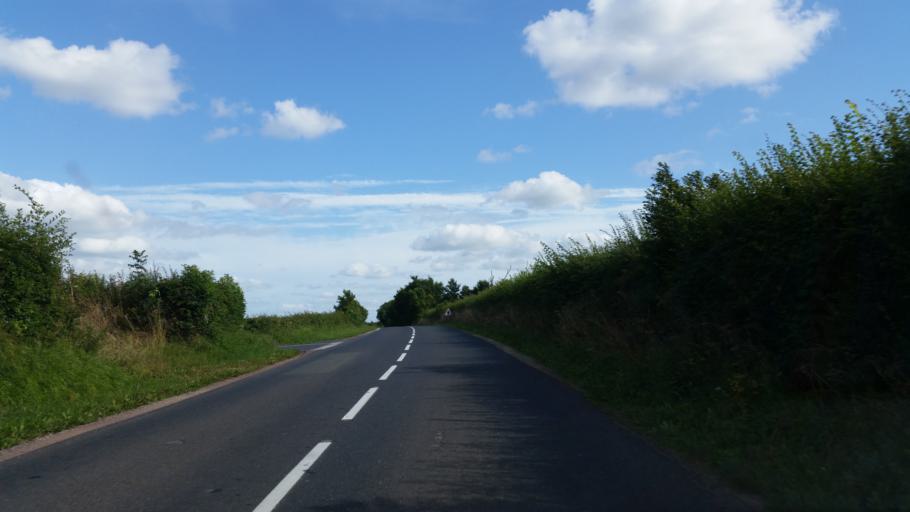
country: FR
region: Lower Normandy
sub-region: Departement de la Manche
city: Sainte-Mere-Eglise
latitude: 49.4504
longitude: -1.2641
